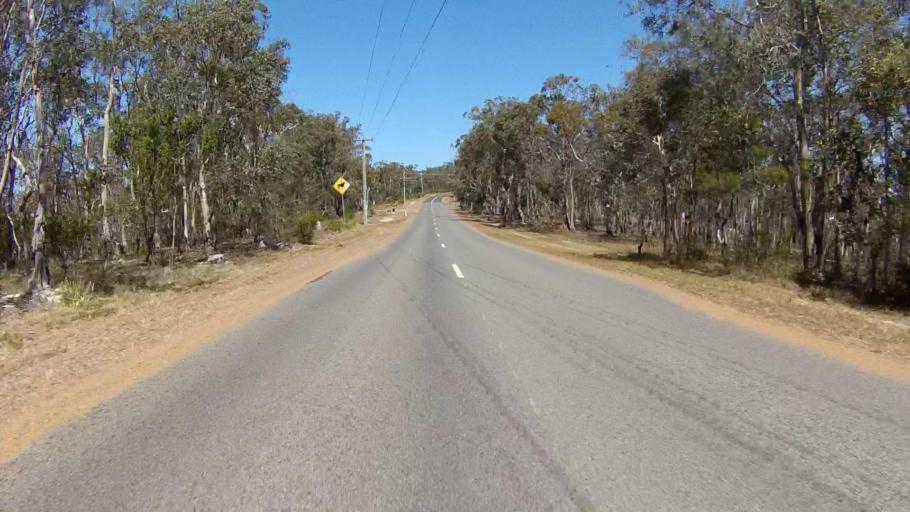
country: AU
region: Tasmania
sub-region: Clarence
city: Sandford
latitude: -43.0057
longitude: 147.4792
